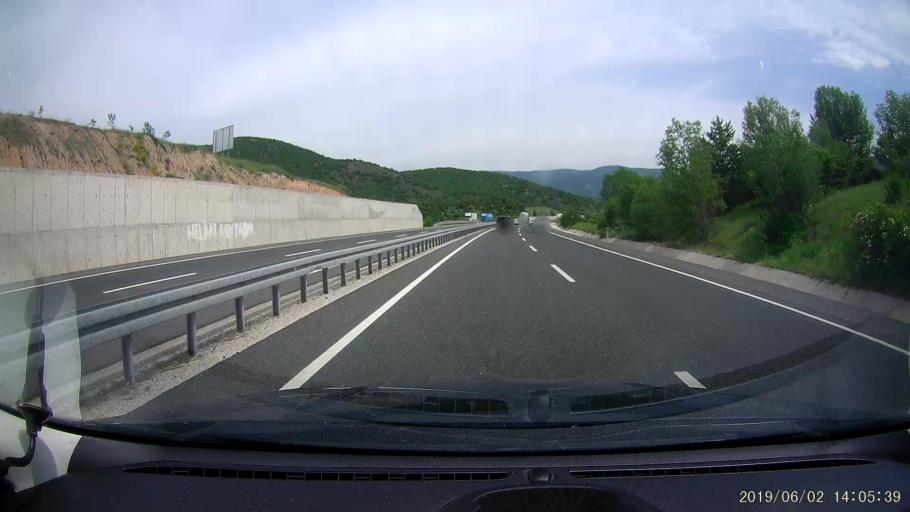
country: TR
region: Cankiri
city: Ilgaz
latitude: 40.8990
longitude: 33.6726
